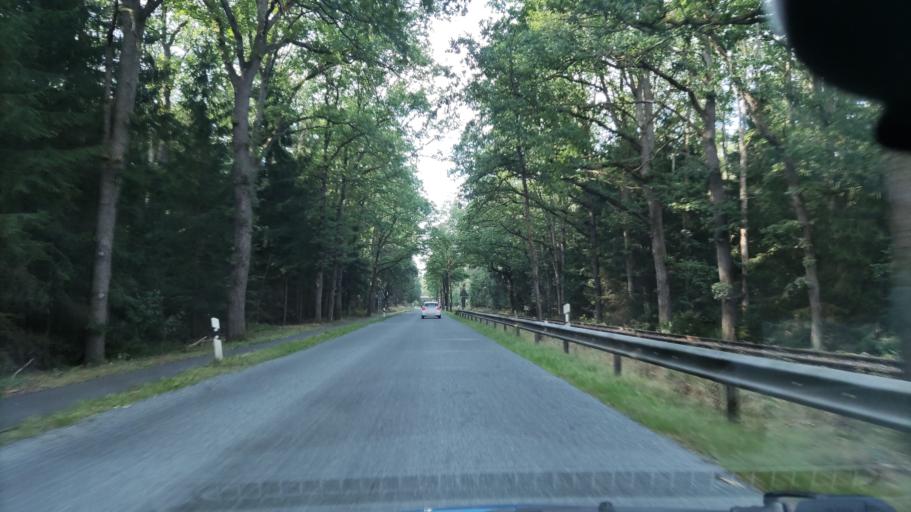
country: DE
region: Lower Saxony
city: Munster
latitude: 52.9829
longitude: 10.1305
